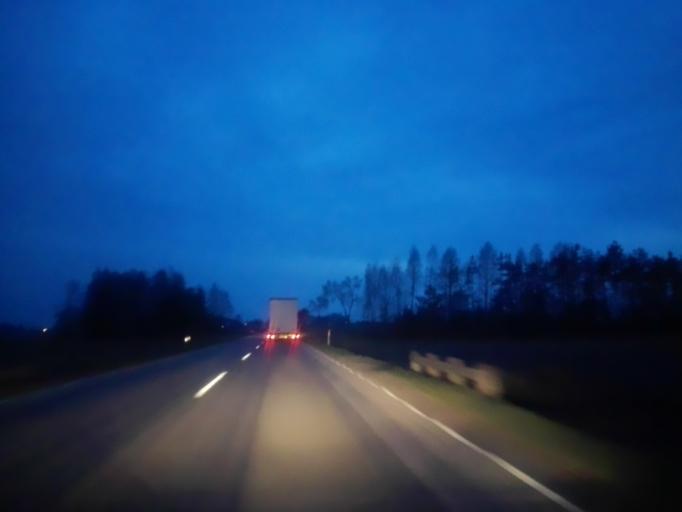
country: PL
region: Podlasie
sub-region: Powiat lomzynski
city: Sniadowo
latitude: 53.0548
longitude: 21.9972
